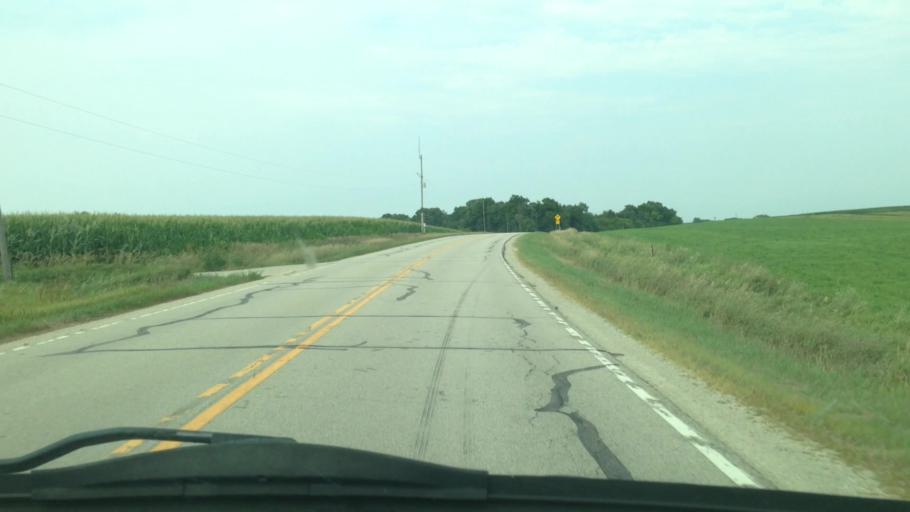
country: US
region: Minnesota
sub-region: Fillmore County
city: Preston
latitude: 43.7633
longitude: -91.9619
